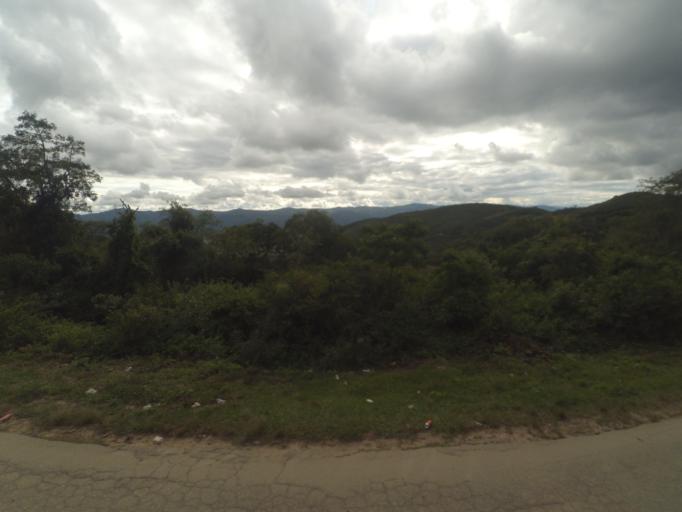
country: BO
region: Santa Cruz
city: Samaipata
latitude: -18.1768
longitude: -63.8625
